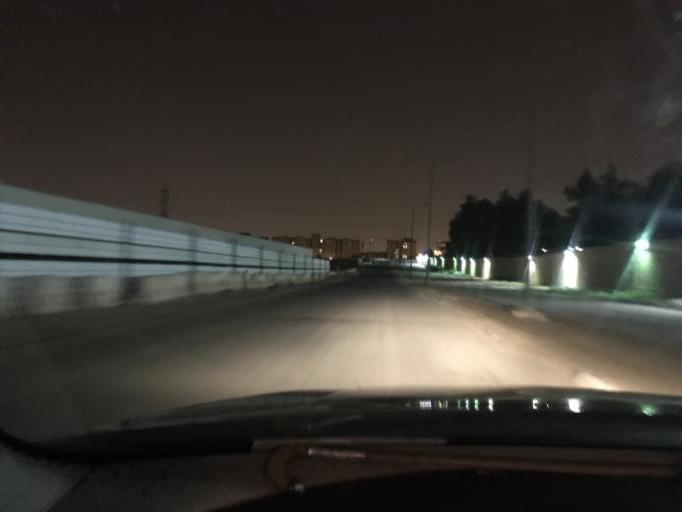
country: SA
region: Ar Riyad
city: Riyadh
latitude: 24.8141
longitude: 46.7164
